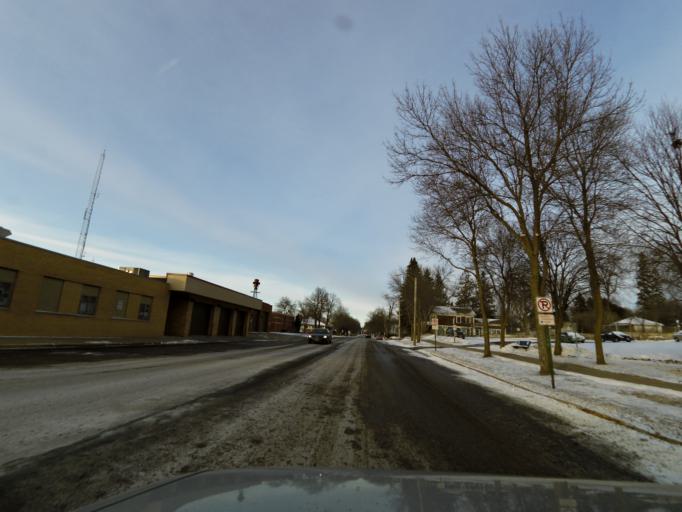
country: US
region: Wisconsin
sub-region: Pierce County
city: River Falls
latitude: 44.8582
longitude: -92.6245
